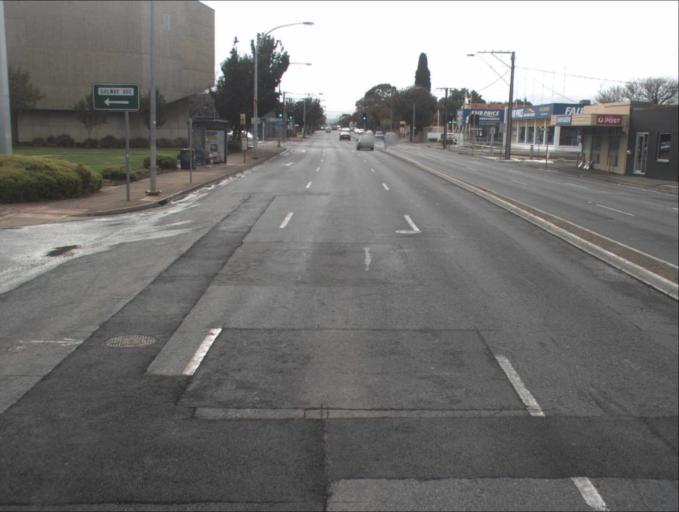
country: AU
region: South Australia
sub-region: Prospect
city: Prospect
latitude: -34.8886
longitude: 138.6142
